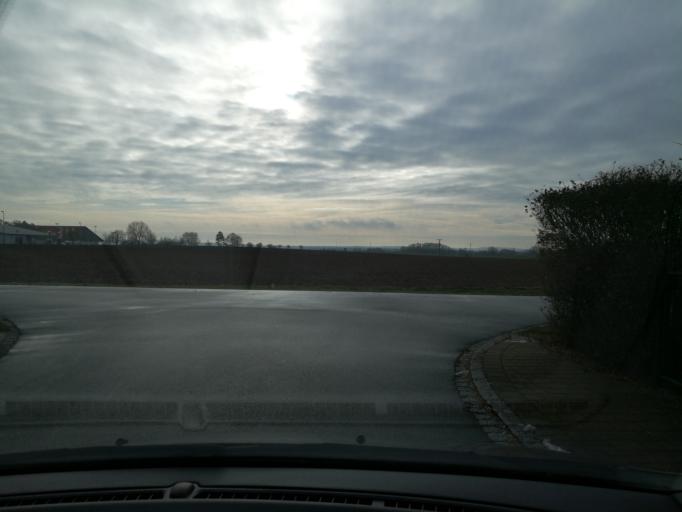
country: DE
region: Bavaria
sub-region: Regierungsbezirk Mittelfranken
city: Obermichelbach
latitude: 49.5268
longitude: 10.9045
